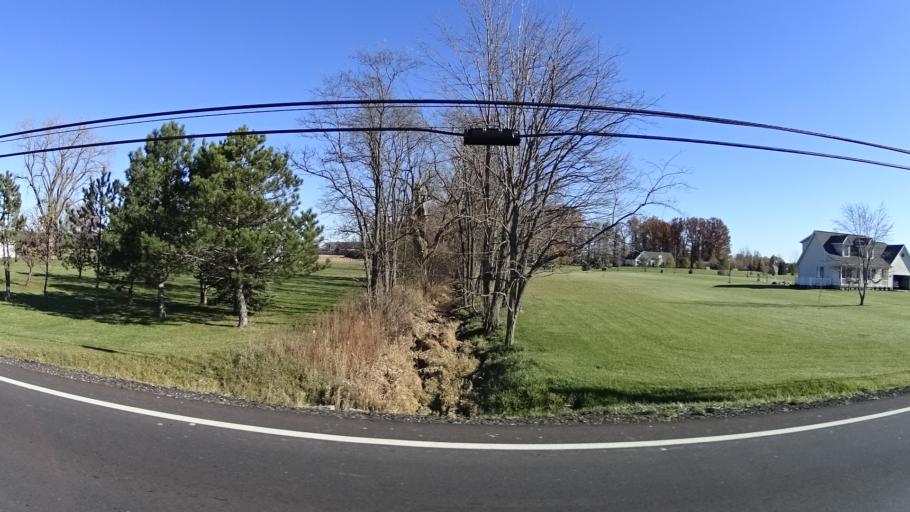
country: US
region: Ohio
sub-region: Lorain County
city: Lagrange
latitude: 41.3030
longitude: -82.1178
